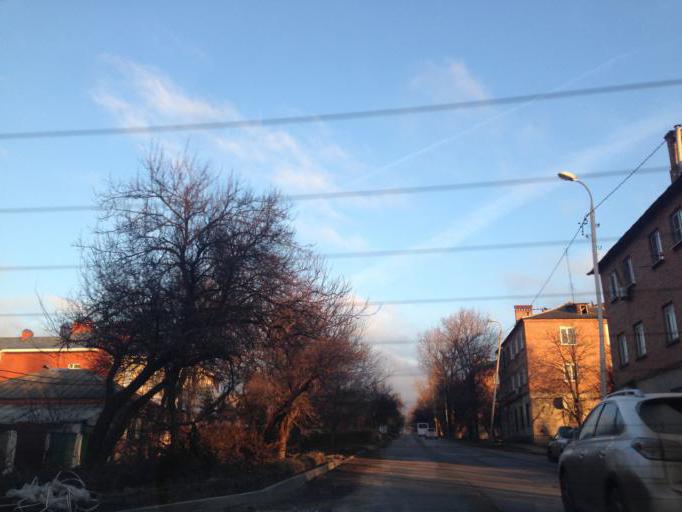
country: RU
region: Rostov
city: Rostov-na-Donu
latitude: 47.2504
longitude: 39.6811
